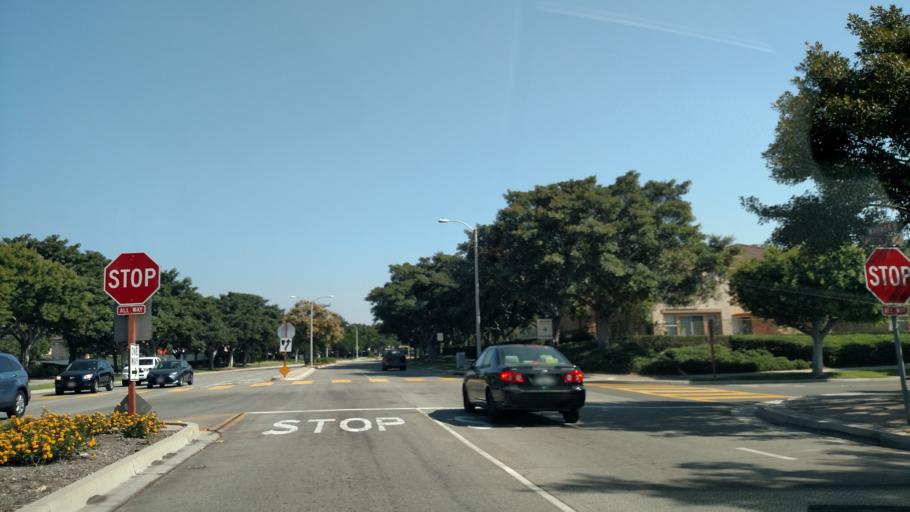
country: US
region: California
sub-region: Orange County
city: Irvine
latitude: 33.6894
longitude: -117.8077
